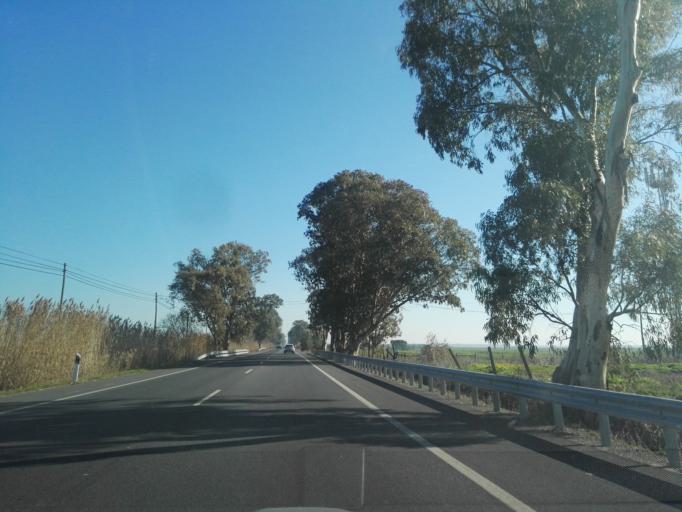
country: PT
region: Santarem
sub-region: Benavente
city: Samora Correia
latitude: 38.9374
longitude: -8.9304
